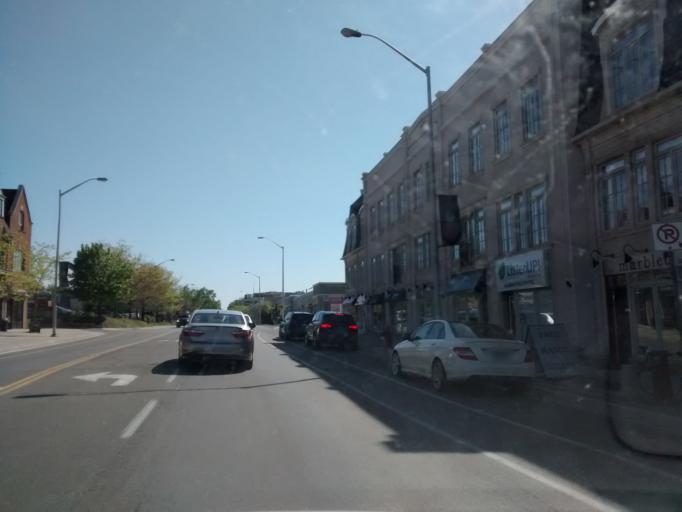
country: CA
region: Ontario
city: Oakville
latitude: 43.4395
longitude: -79.6750
